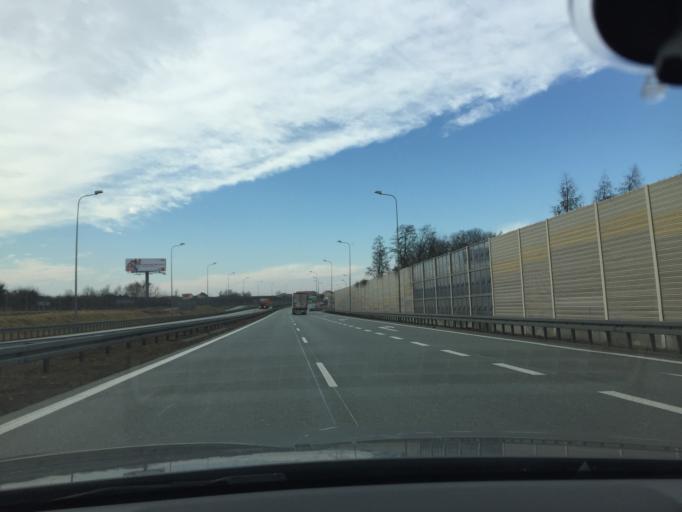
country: PL
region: Lodz Voivodeship
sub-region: Powiat skierniewicki
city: Kowiesy
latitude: 51.8875
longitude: 20.4168
